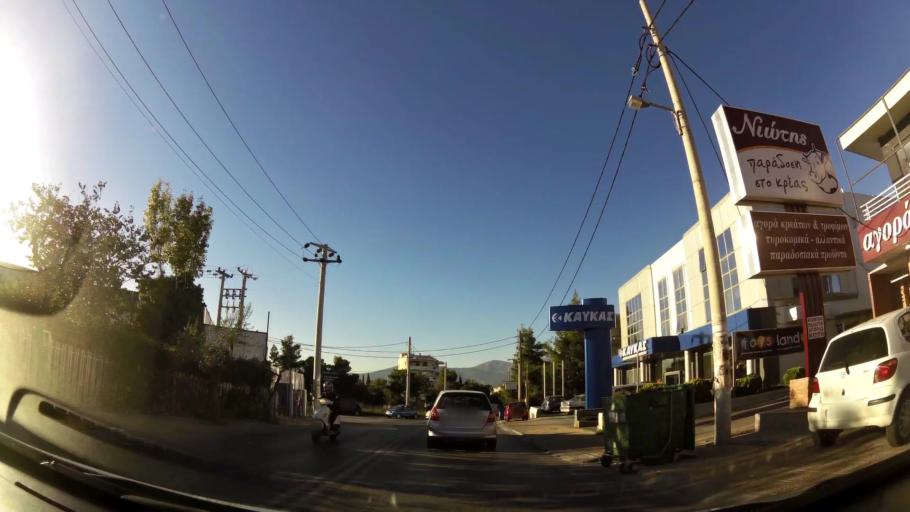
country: GR
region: Attica
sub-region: Nomarchia Athinas
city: Lykovrysi
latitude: 38.0613
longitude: 23.7838
